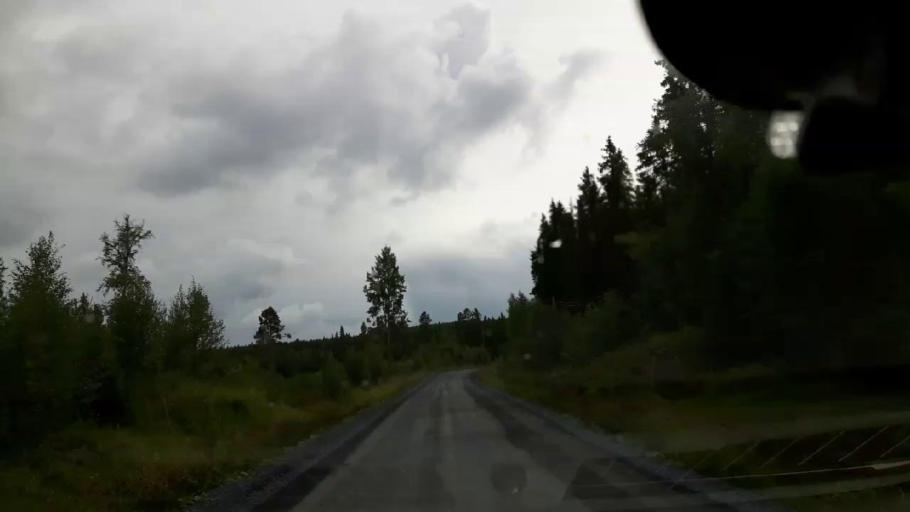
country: SE
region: Jaemtland
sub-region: Krokoms Kommun
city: Valla
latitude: 63.3725
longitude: 13.8826
